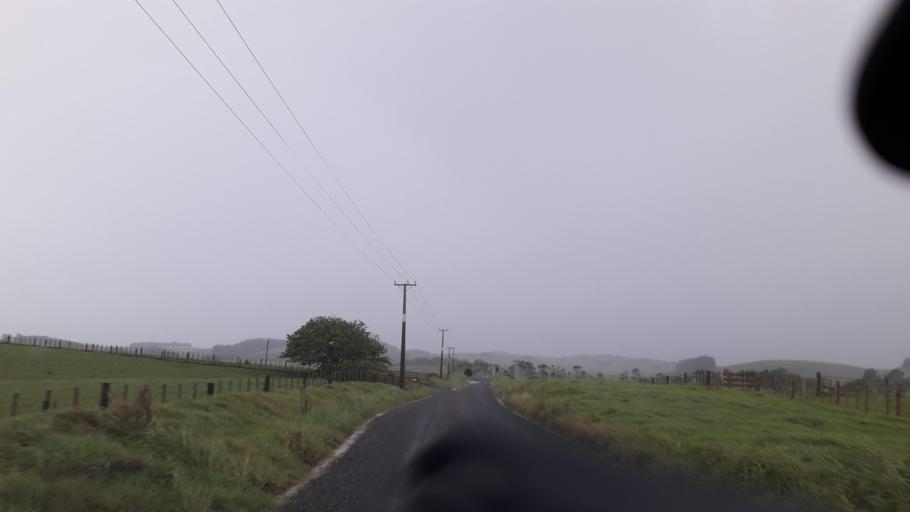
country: NZ
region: Northland
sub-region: Far North District
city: Kerikeri
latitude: -35.1453
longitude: 174.0373
